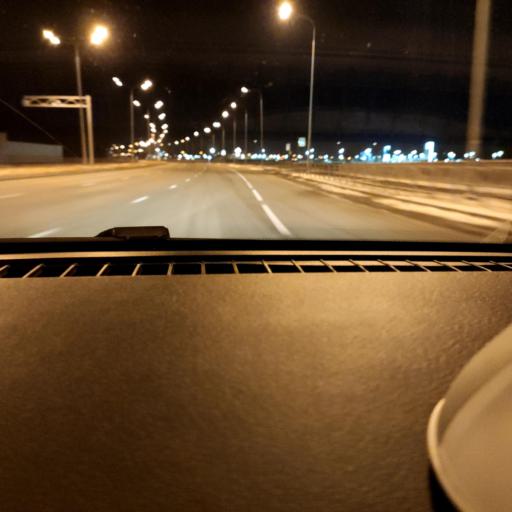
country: RU
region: Samara
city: Samara
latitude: 53.2808
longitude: 50.2426
